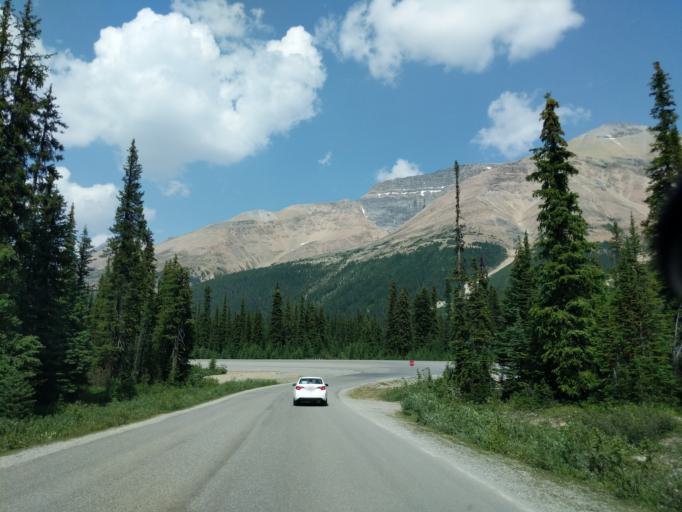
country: CA
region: Alberta
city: Lake Louise
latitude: 51.7192
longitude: -116.4951
